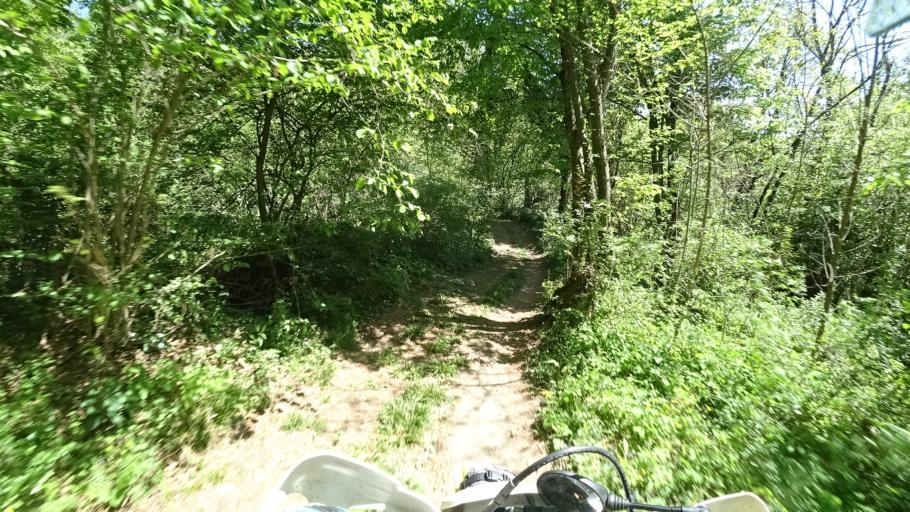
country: HR
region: Zagrebacka
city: Jablanovec
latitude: 45.8501
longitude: 15.8568
